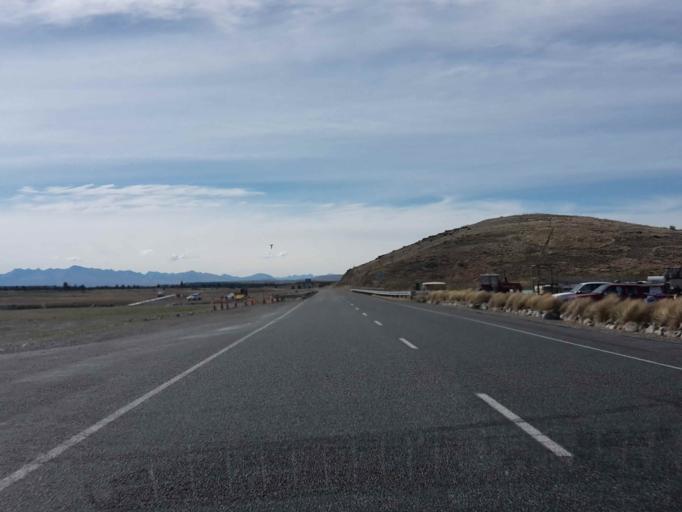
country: NZ
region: Otago
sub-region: Queenstown-Lakes District
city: Wanaka
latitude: -44.2911
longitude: 170.0836
